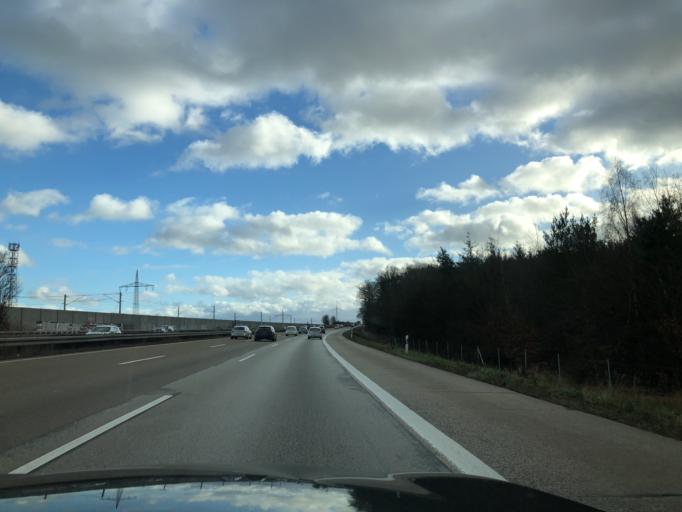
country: DE
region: Hesse
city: Bad Camberg
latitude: 50.3261
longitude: 8.2153
